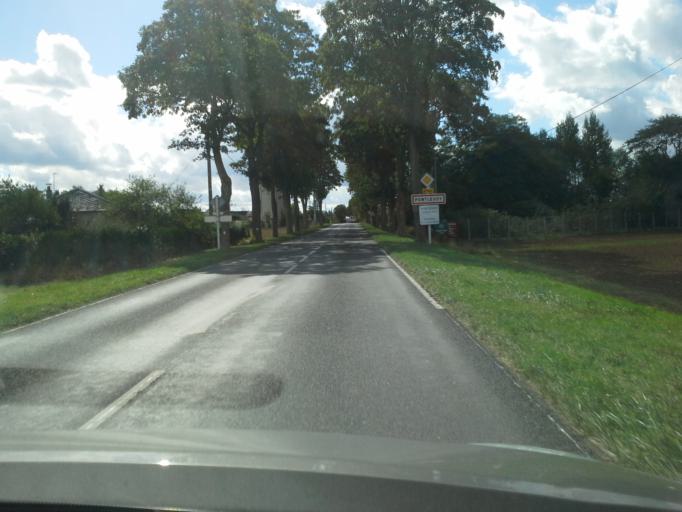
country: FR
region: Centre
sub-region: Departement du Loir-et-Cher
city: Pontlevoy
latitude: 47.3994
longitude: 1.2622
